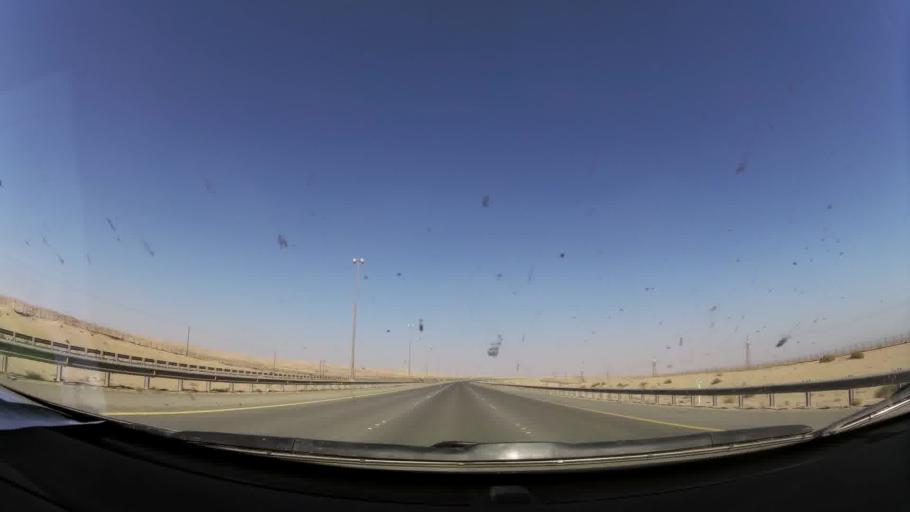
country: KW
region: Muhafazat al Jahra'
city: Al Jahra'
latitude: 29.5107
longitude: 47.8020
